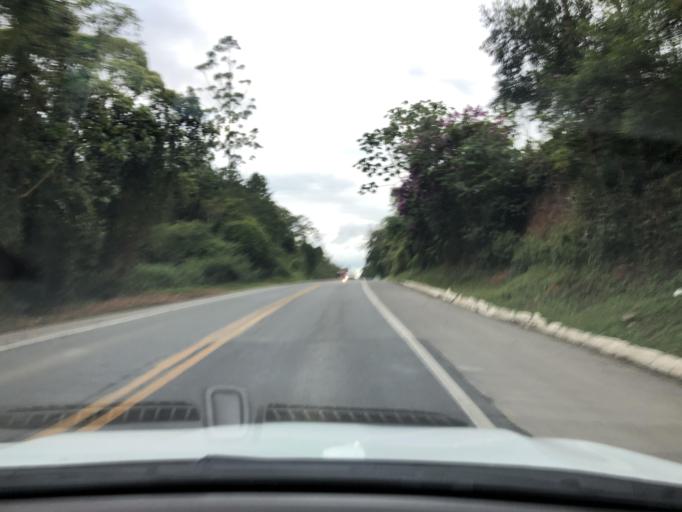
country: BR
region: Santa Catarina
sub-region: Joinville
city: Joinville
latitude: -26.4334
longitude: -48.8033
